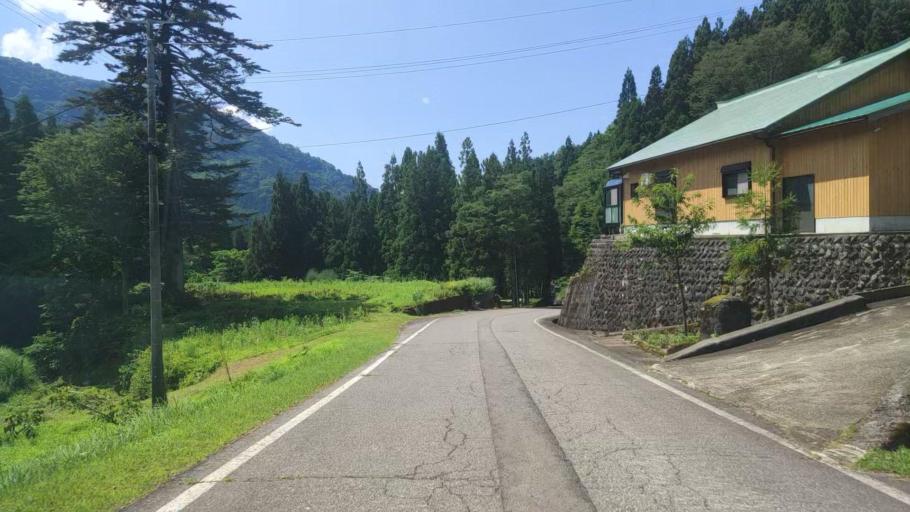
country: JP
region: Fukui
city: Katsuyama
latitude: 36.1242
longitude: 136.5077
